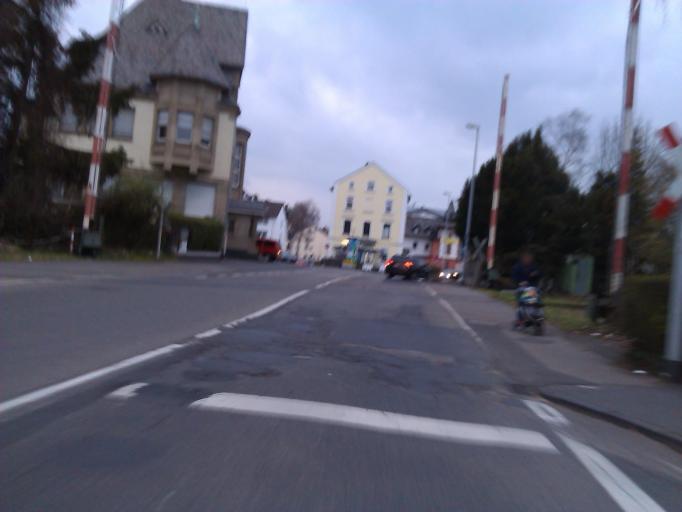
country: DE
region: Rheinland-Pfalz
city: Lahnstein
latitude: 50.3046
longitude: 7.6039
